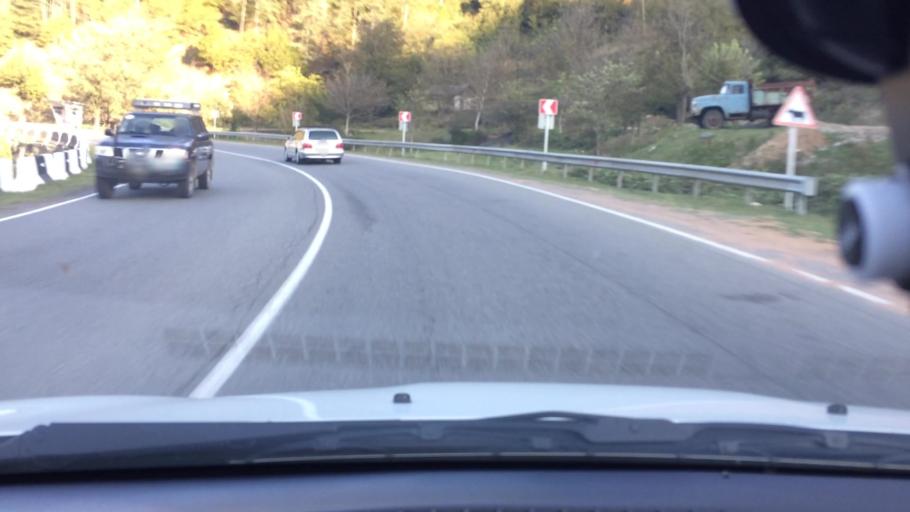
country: GE
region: Imereti
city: Kharagauli
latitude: 42.1084
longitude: 43.3087
